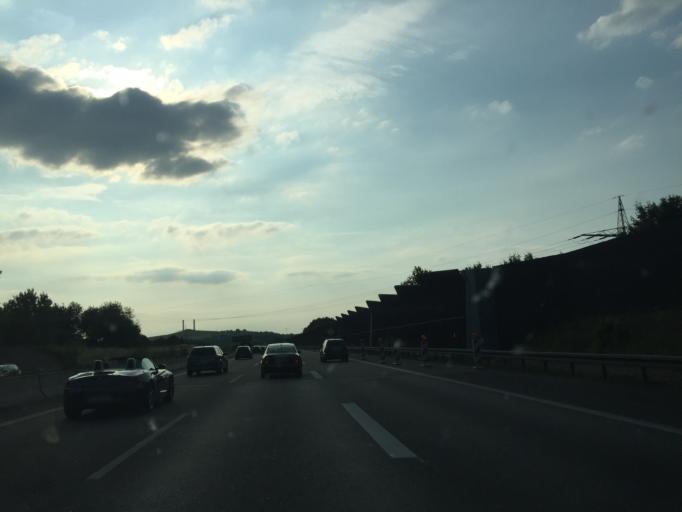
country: DE
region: Baden-Wuerttemberg
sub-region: Regierungsbezirk Stuttgart
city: Erlenbach
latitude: 49.1642
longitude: 9.2730
